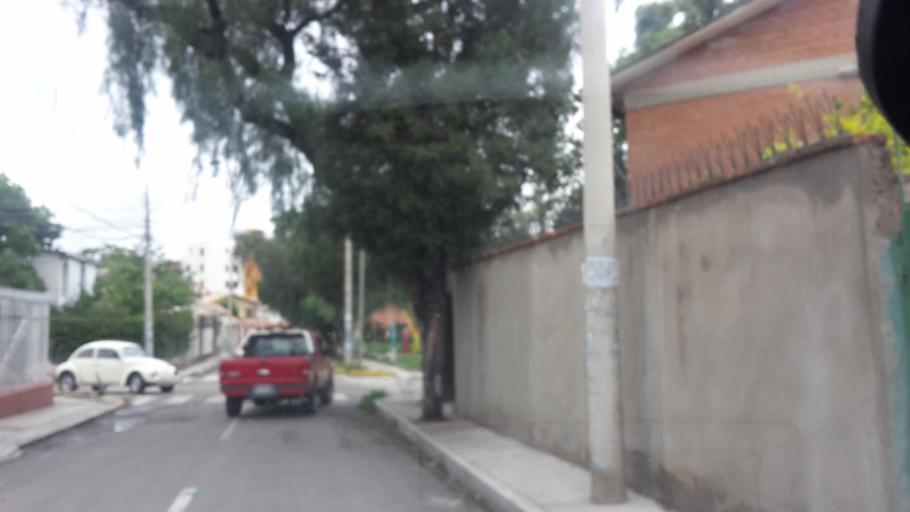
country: BO
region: Cochabamba
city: Cochabamba
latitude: -17.3634
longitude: -66.1765
